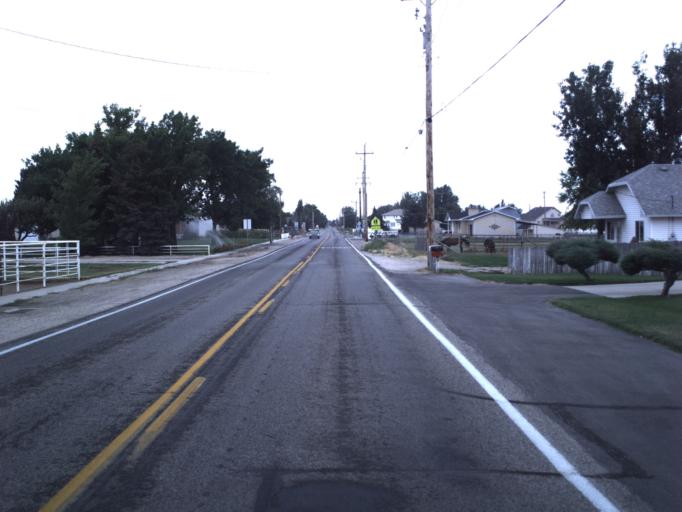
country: US
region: Utah
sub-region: Davis County
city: West Point
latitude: 41.1202
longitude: -112.1126
